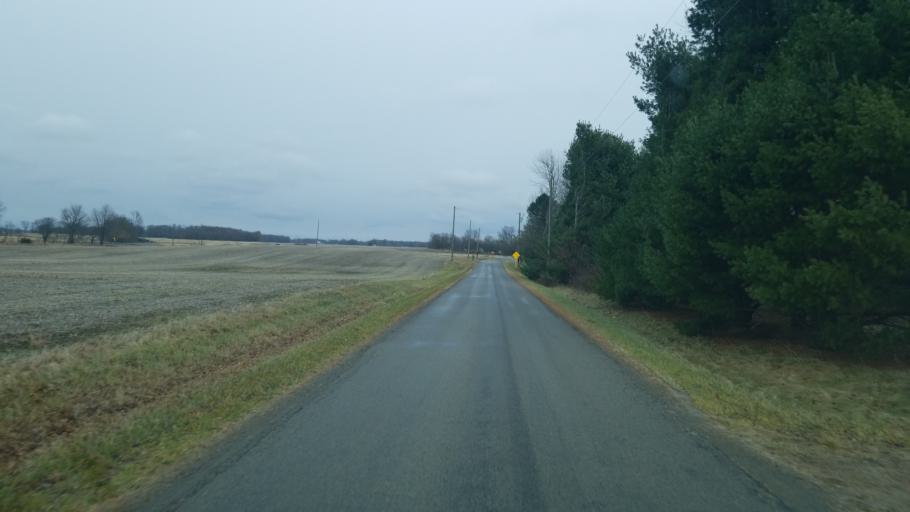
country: US
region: Ohio
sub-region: Union County
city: Marysville
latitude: 40.3061
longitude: -83.2977
